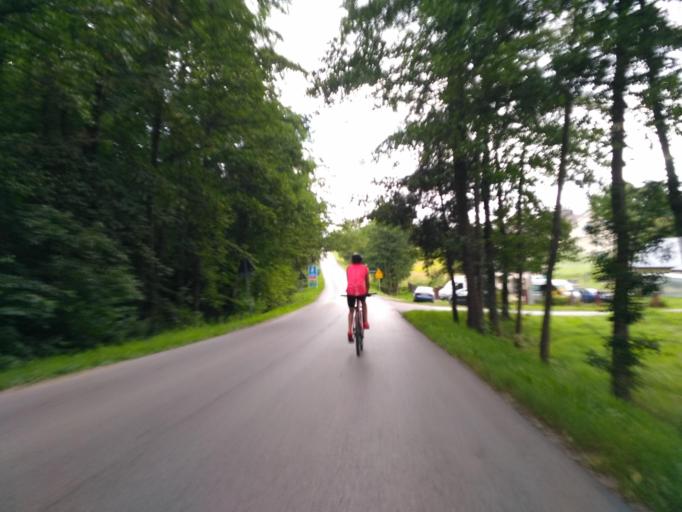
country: PL
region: Subcarpathian Voivodeship
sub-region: Powiat rzeszowski
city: Lecka
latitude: 49.9145
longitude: 22.0248
